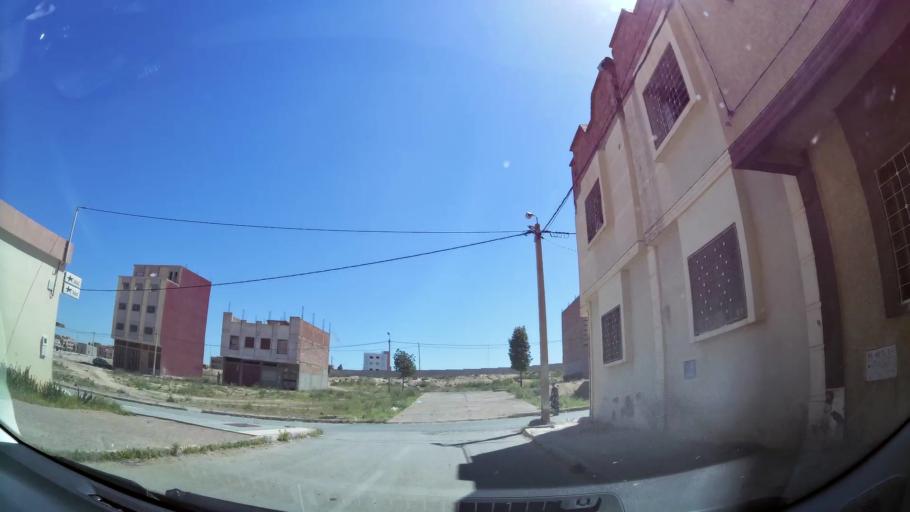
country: MA
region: Oriental
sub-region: Oujda-Angad
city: Oujda
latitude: 34.6551
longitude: -1.8732
